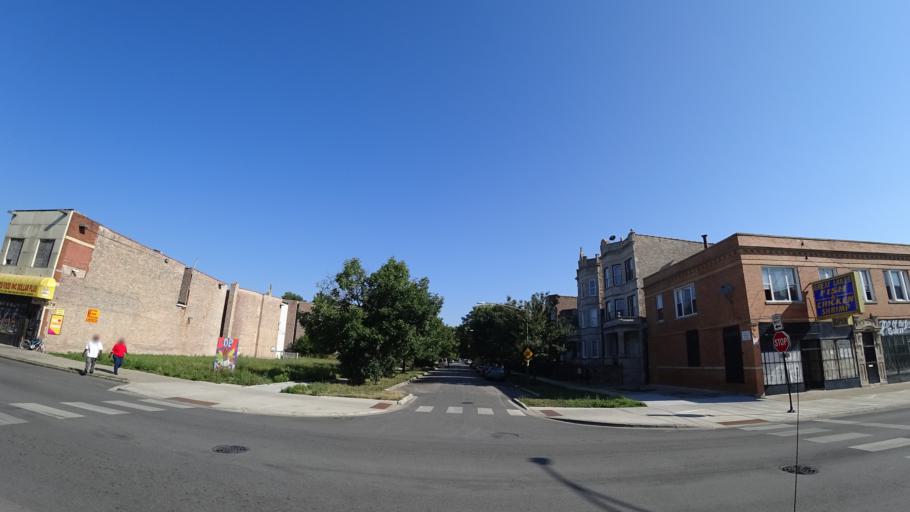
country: US
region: Illinois
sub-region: Cook County
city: Cicero
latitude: 41.8589
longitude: -87.7164
